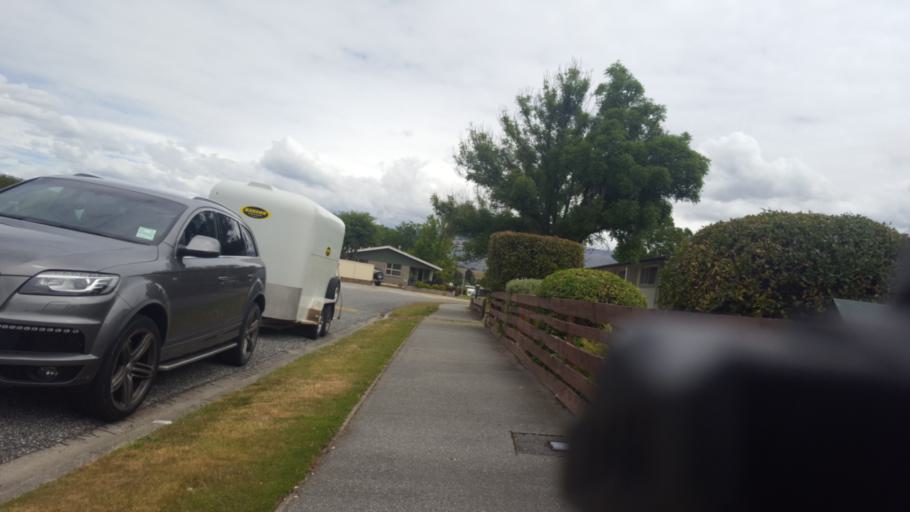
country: NZ
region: Otago
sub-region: Queenstown-Lakes District
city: Wanaka
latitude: -45.2465
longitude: 169.3805
